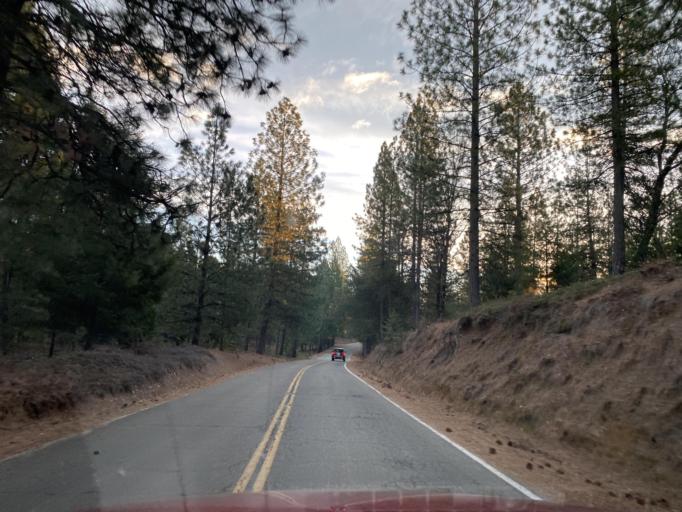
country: US
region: California
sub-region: Amador County
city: Pioneer
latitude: 38.4993
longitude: -120.6275
